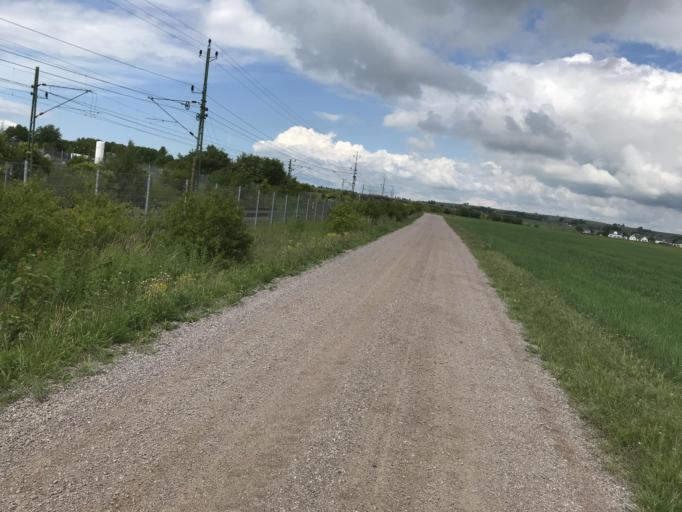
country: SE
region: Skane
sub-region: Landskrona
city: Landskrona
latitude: 55.8893
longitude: 12.8561
